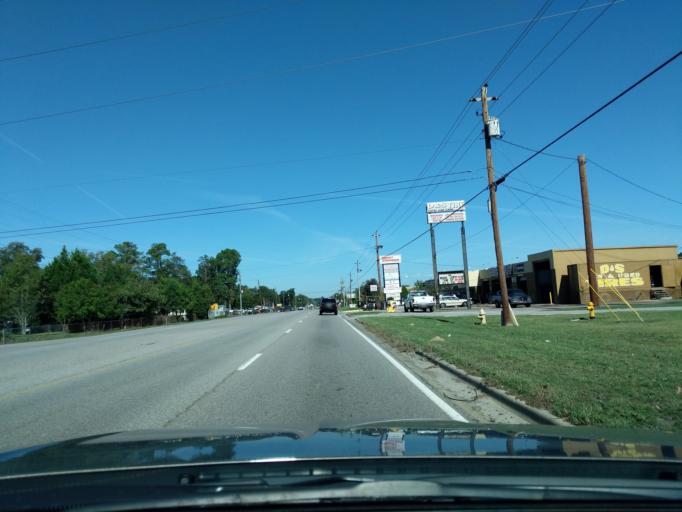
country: US
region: Georgia
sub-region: Richmond County
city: Augusta
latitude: 33.4066
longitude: -82.0062
